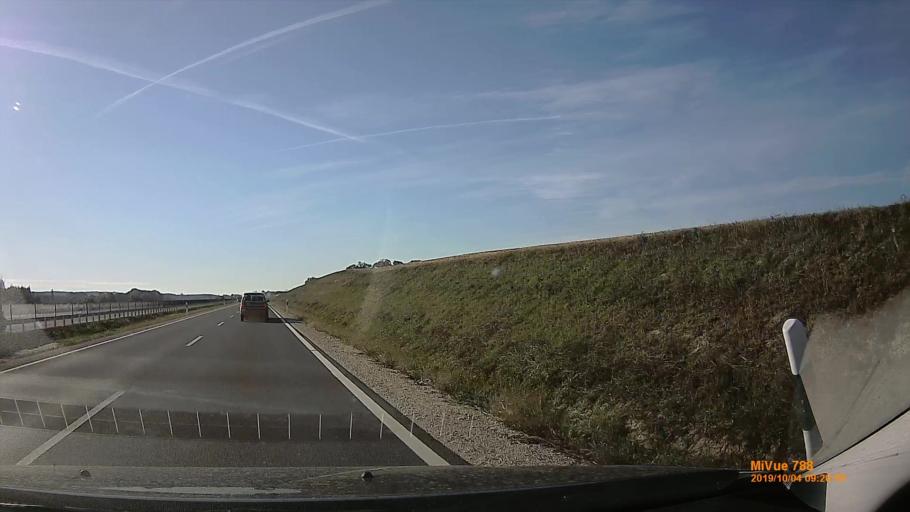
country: HU
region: Somogy
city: Karad
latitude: 46.5681
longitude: 17.8069
